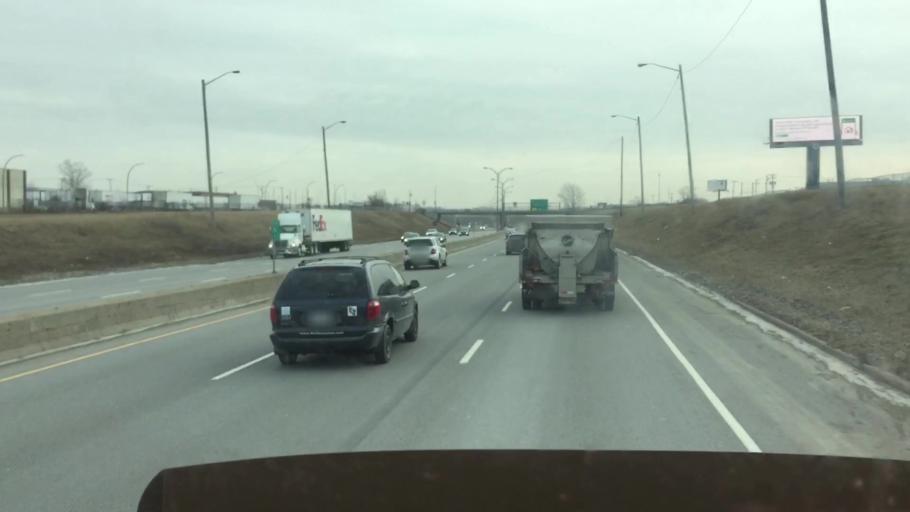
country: CA
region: Quebec
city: Dorval
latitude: 45.4838
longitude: -73.7269
